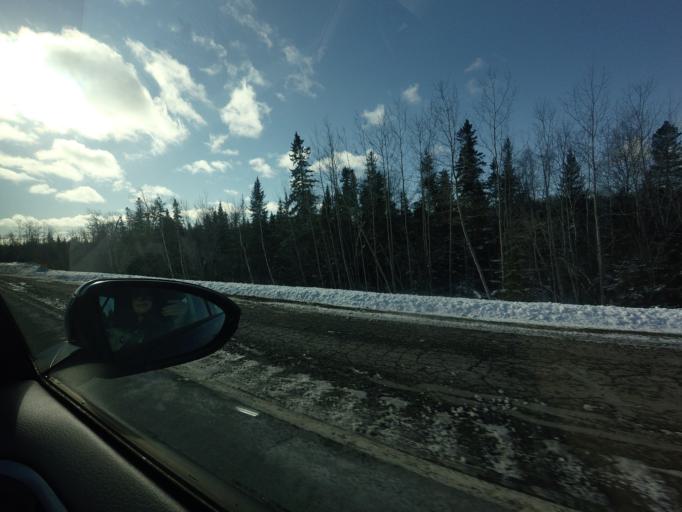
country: CA
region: New Brunswick
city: Fredericton
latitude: 45.8874
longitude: -66.6422
